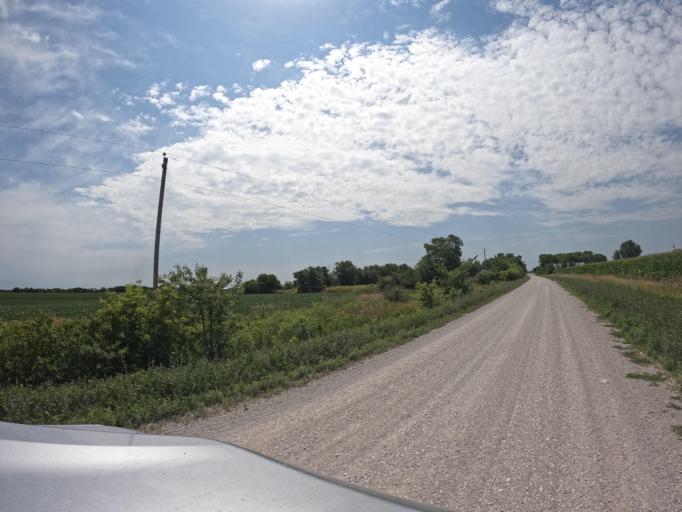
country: US
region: Iowa
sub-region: Appanoose County
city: Centerville
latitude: 40.8150
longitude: -92.9448
